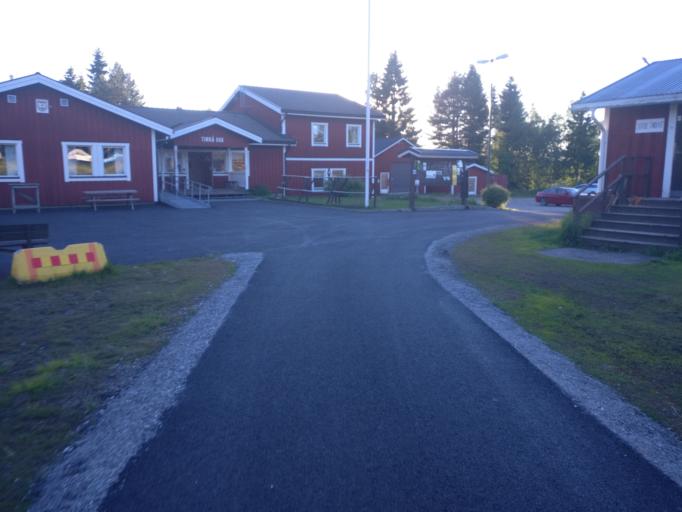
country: SE
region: Vaesternorrland
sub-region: Timra Kommun
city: Timra
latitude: 62.4616
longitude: 17.2933
